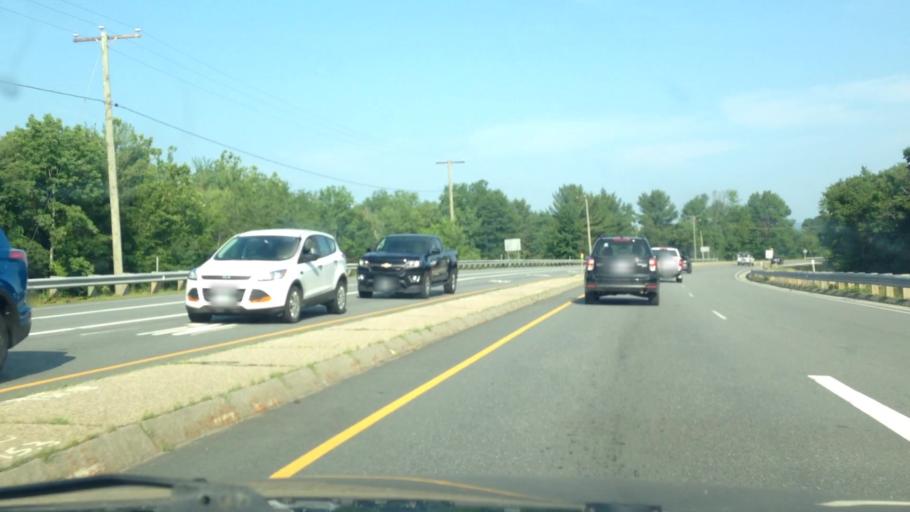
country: US
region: New Hampshire
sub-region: Cheshire County
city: Keene
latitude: 42.9157
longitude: -72.2633
